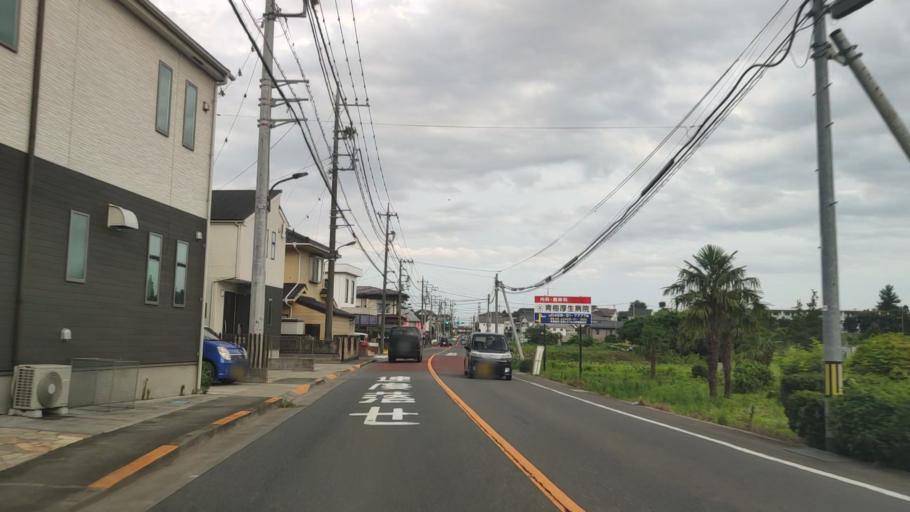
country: JP
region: Saitama
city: Hanno
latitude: 35.8076
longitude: 139.3042
